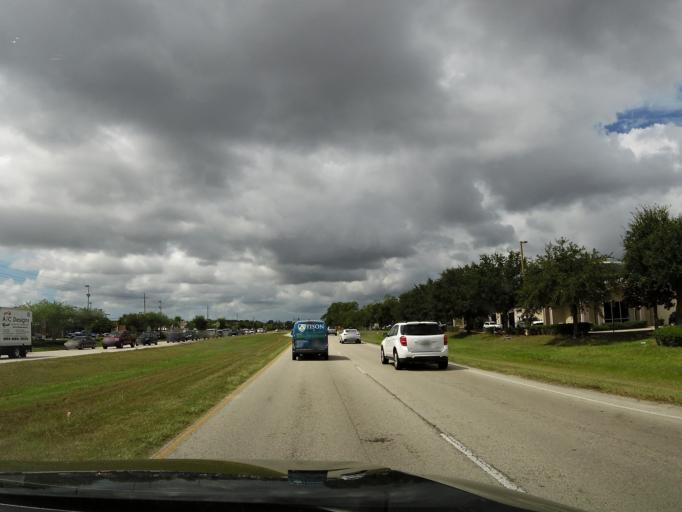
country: US
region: Florida
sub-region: Clay County
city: Lakeside
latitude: 30.1023
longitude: -81.7125
